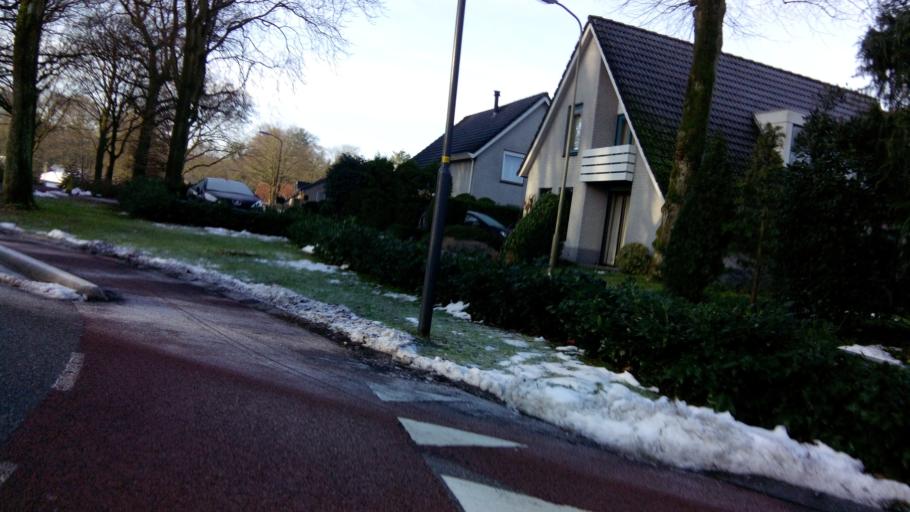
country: NL
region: Gelderland
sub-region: Gemeente Groesbeek
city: Berg en Dal
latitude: 51.8186
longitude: 5.9239
